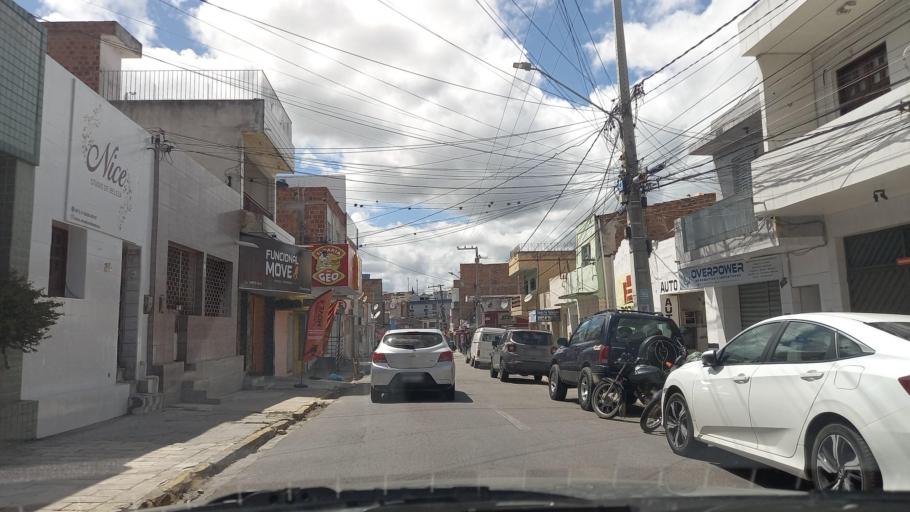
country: BR
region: Pernambuco
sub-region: Caruaru
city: Caruaru
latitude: -8.2840
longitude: -35.9644
